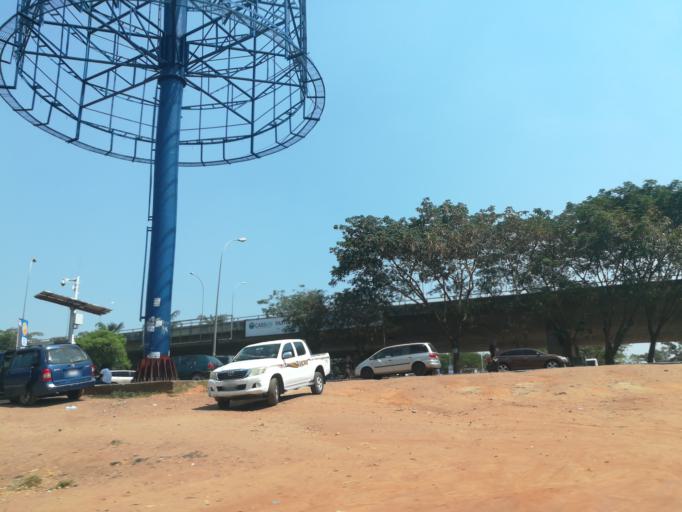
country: NG
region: Abuja Federal Capital Territory
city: Abuja
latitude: 9.0666
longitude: 7.4512
